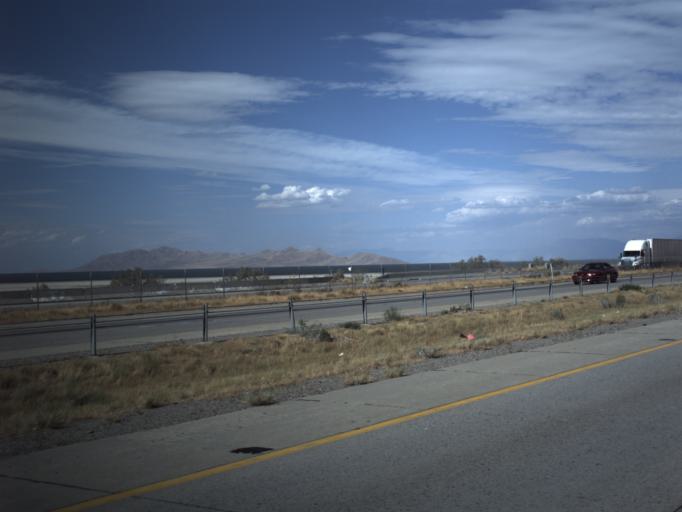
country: US
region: Utah
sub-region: Tooele County
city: Stansbury park
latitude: 40.7148
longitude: -112.2402
